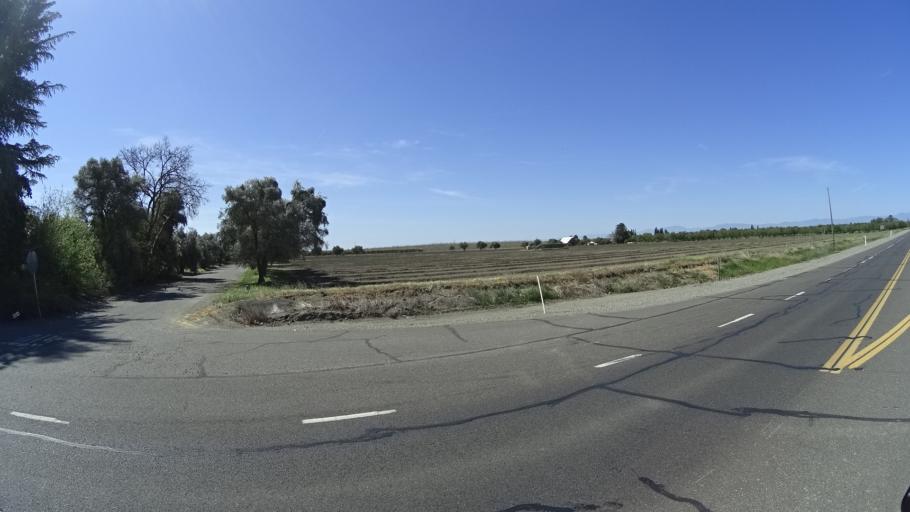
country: US
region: California
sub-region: Glenn County
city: Orland
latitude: 39.7470
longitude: -122.1138
